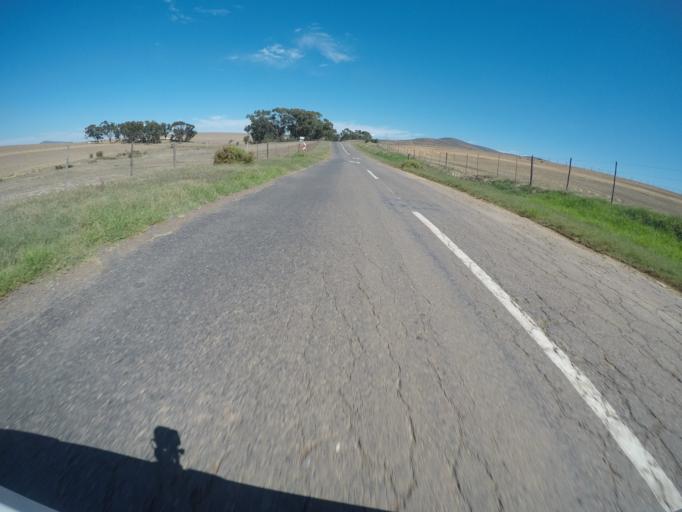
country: ZA
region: Western Cape
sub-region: City of Cape Town
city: Atlantis
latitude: -33.6968
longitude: 18.5908
